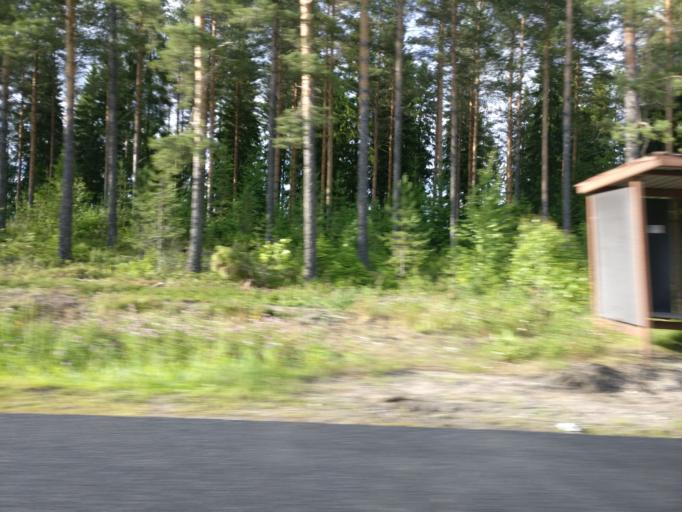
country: FI
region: Northern Savo
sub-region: Kuopio
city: Vehmersalmi
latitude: 62.9271
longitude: 28.0892
